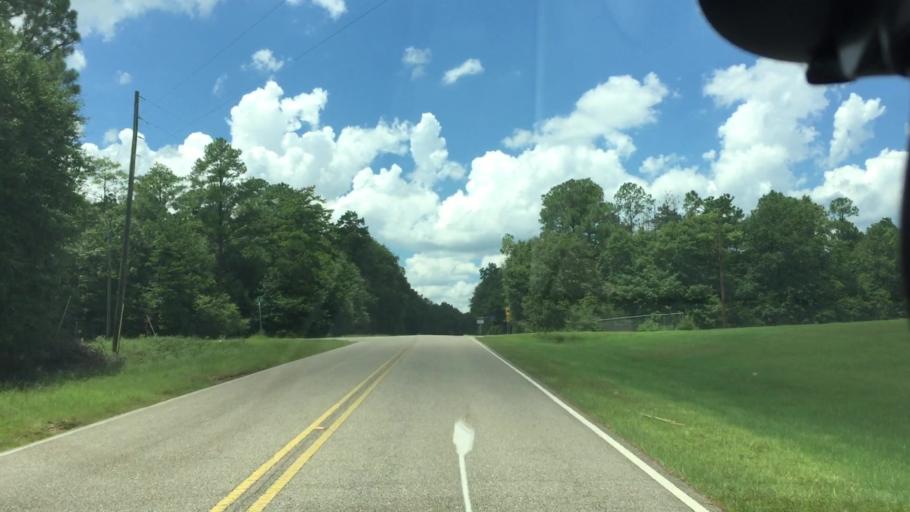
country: US
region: Alabama
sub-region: Coffee County
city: New Brockton
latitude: 31.4092
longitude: -85.8479
